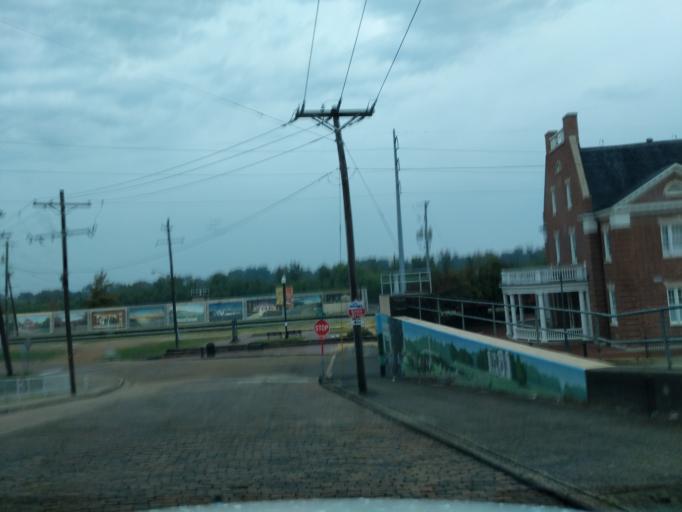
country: US
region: Mississippi
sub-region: Warren County
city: Vicksburg
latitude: 32.3522
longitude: -90.8824
